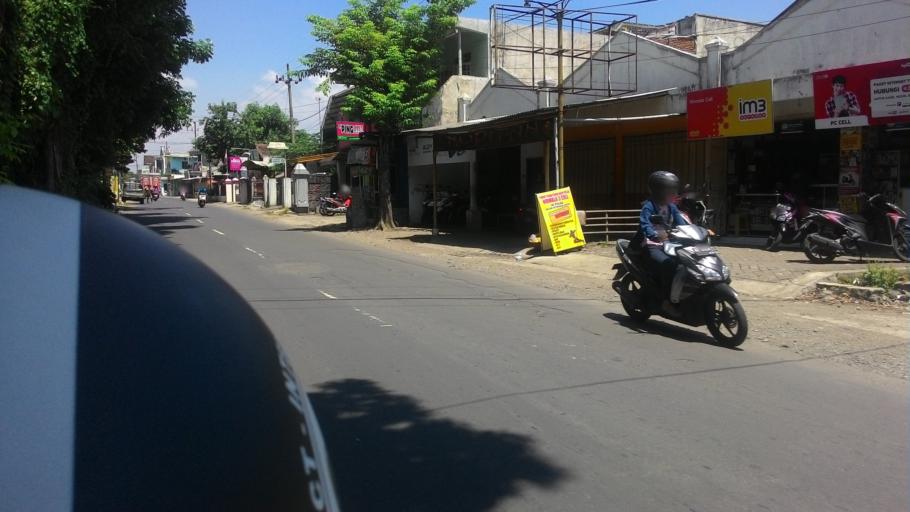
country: ID
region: East Java
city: Tegalgede Kulon
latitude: -8.1595
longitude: 113.7180
